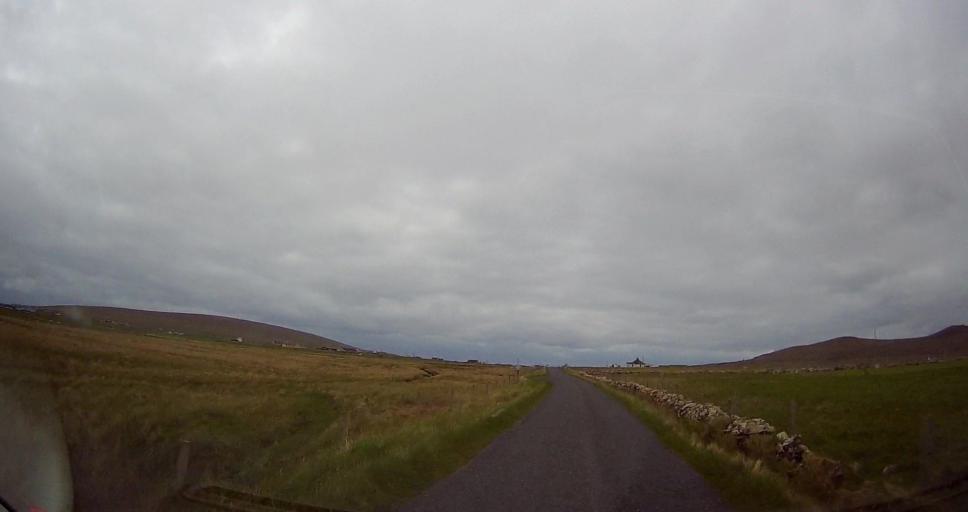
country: GB
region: Scotland
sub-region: Shetland Islands
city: Shetland
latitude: 60.7934
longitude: -0.8520
